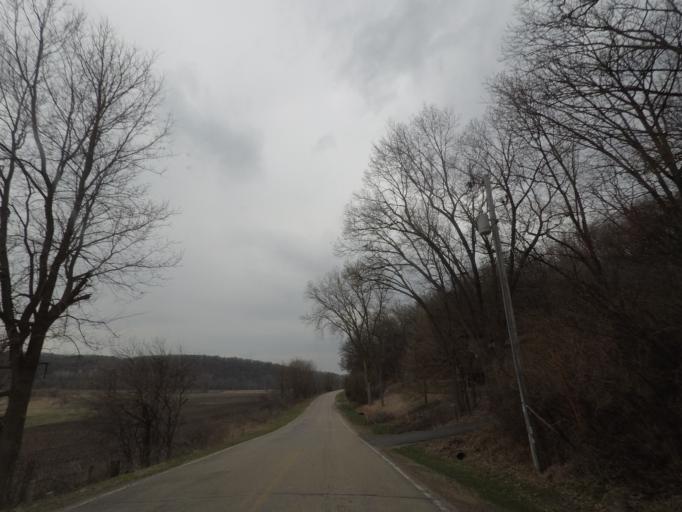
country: US
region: Wisconsin
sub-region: Dane County
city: Cross Plains
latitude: 43.0987
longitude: -89.6010
